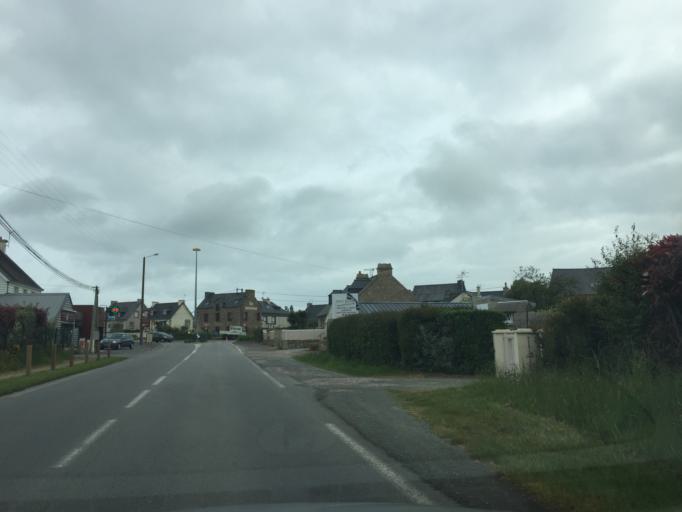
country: FR
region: Brittany
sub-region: Departement des Cotes-d'Armor
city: Crehen
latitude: 48.5816
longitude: -2.2345
